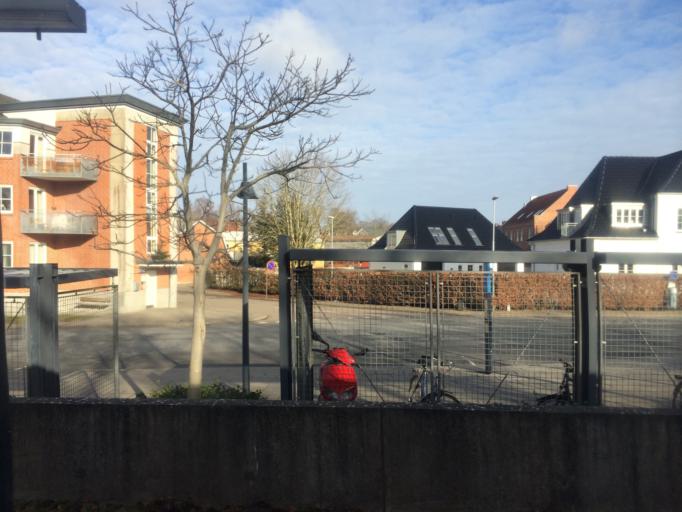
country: DK
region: South Denmark
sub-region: Vejle Kommune
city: Give
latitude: 55.8433
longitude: 9.2355
